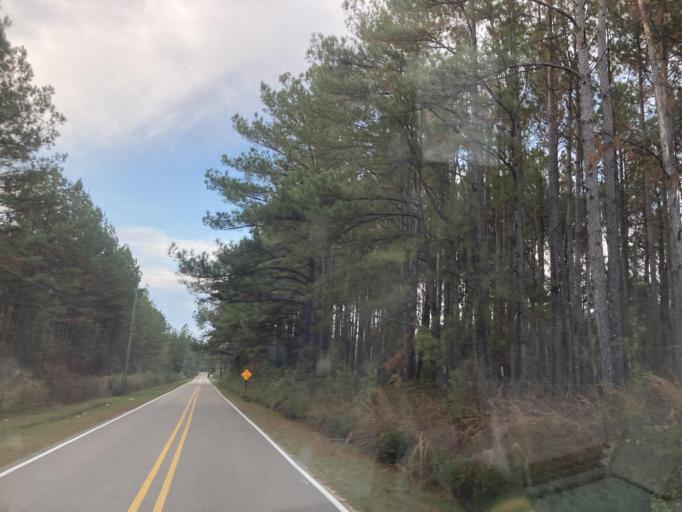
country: US
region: Mississippi
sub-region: Lamar County
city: Purvis
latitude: 31.1864
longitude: -89.3640
